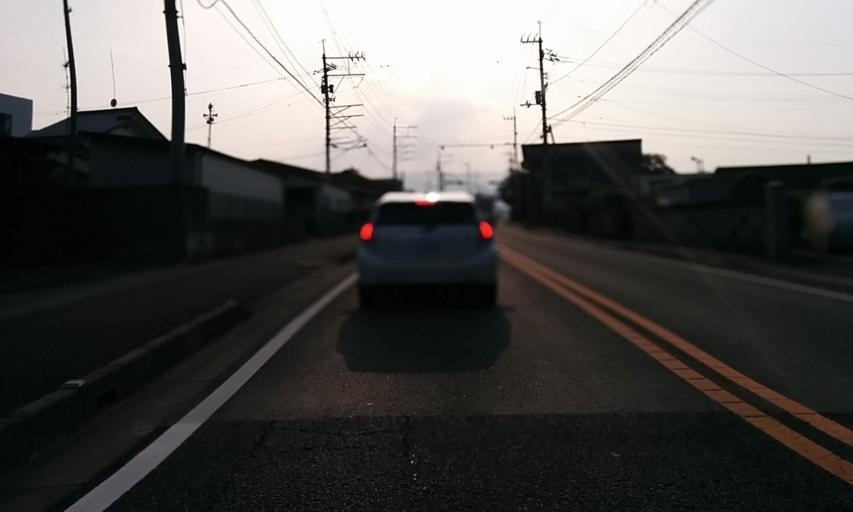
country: JP
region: Ehime
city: Saijo
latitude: 33.8955
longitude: 133.1290
